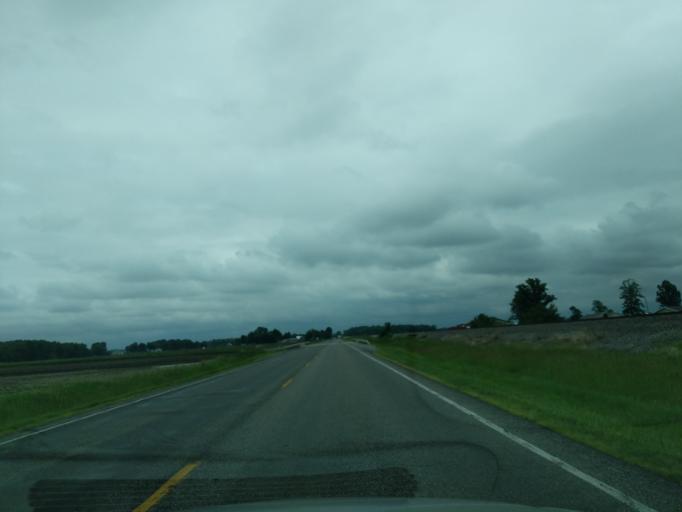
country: US
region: Indiana
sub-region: Madison County
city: Elwood
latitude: 40.2780
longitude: -85.8903
